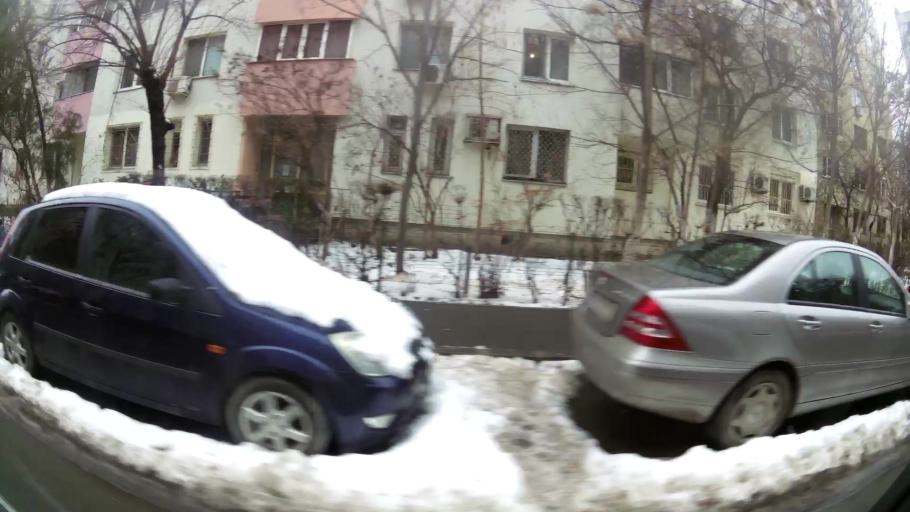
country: RO
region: Ilfov
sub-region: Comuna Chiajna
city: Rosu
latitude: 44.4169
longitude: 26.0465
